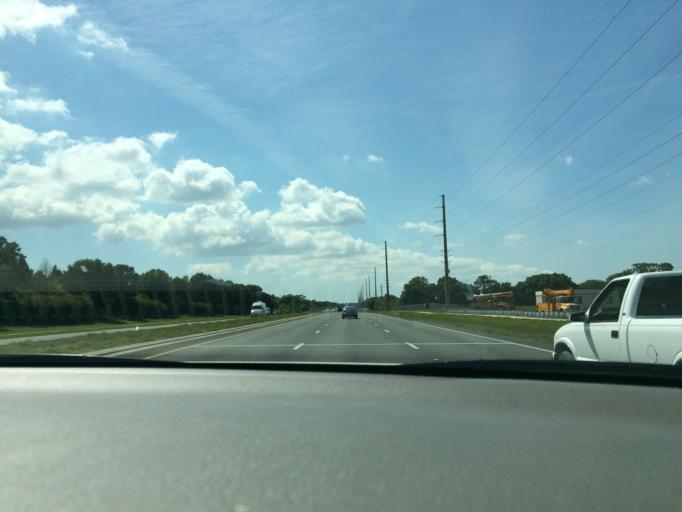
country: US
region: Florida
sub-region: Sarasota County
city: The Meadows
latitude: 27.4321
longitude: -82.4051
